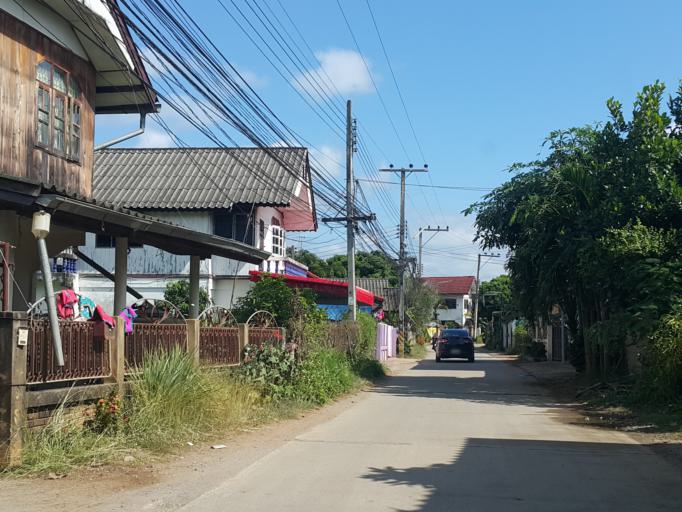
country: TH
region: Lamphun
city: Ban Thi
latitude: 18.5796
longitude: 99.0818
